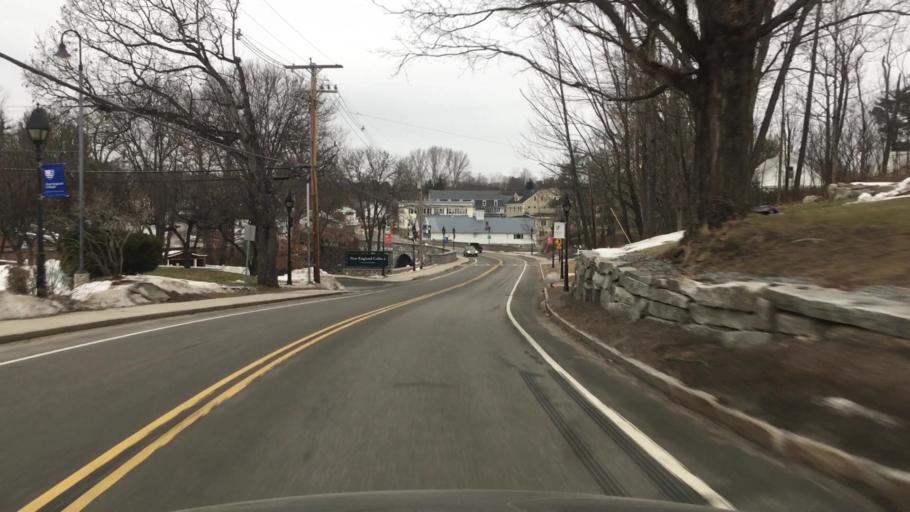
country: US
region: New Hampshire
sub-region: Merrimack County
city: Henniker
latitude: 43.1771
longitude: -71.8220
